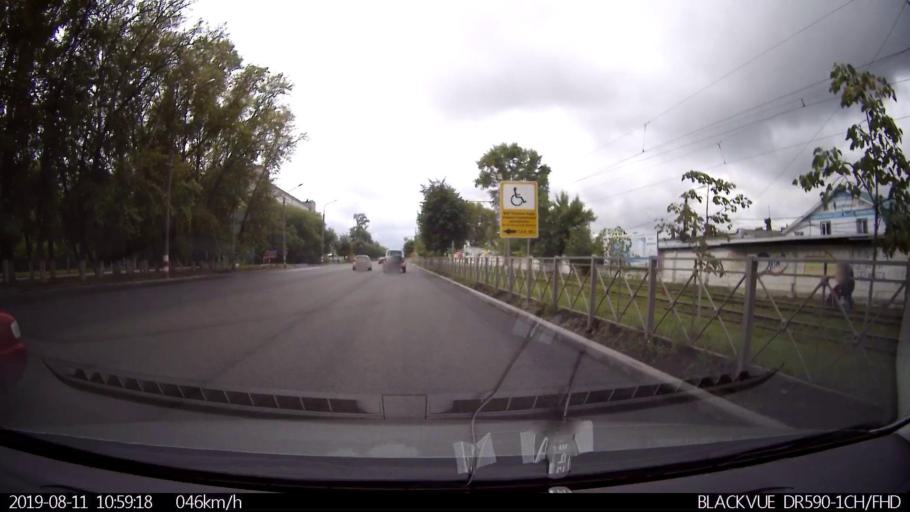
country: RU
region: Ulyanovsk
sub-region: Ulyanovskiy Rayon
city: Ulyanovsk
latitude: 54.2512
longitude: 48.3161
